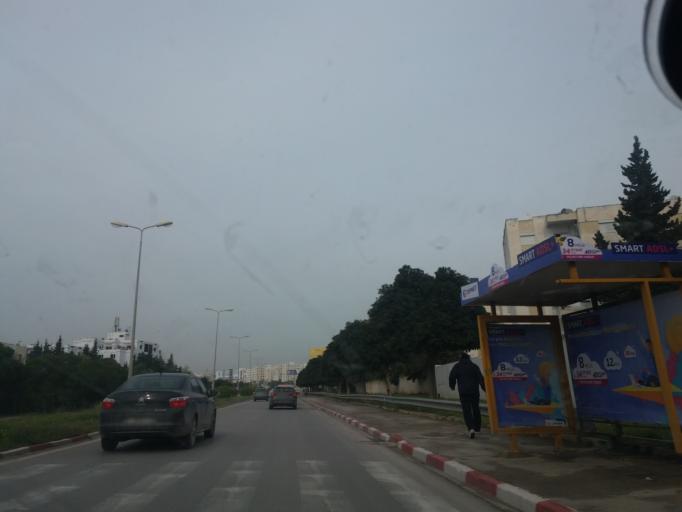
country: TN
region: Tunis
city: Tunis
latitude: 36.8489
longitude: 10.1574
